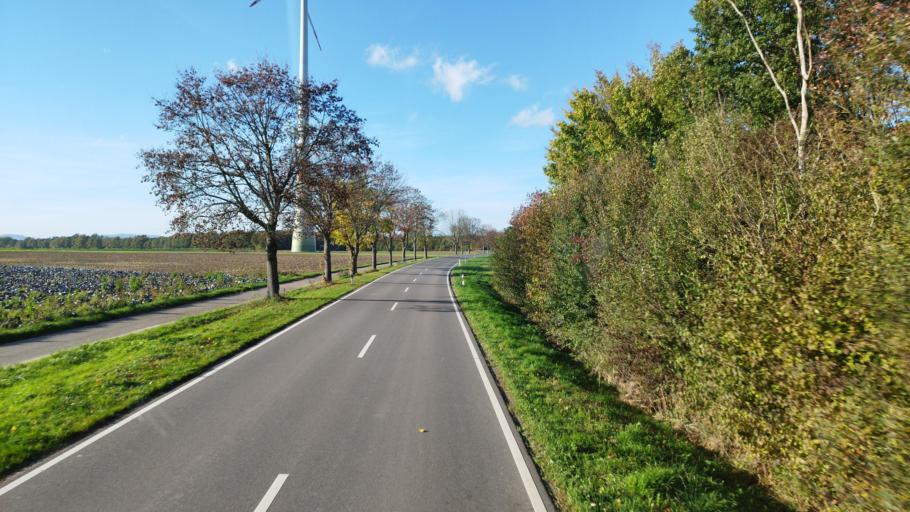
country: DE
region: Rheinland-Pfalz
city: Hatzenbuhl
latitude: 49.1239
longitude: 8.2326
